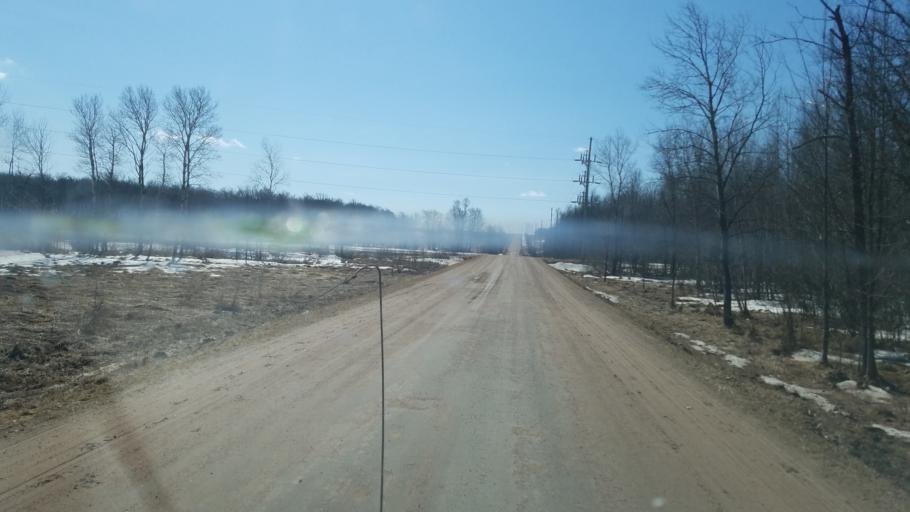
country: US
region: Wisconsin
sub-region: Clark County
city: Loyal
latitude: 44.6070
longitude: -90.3967
